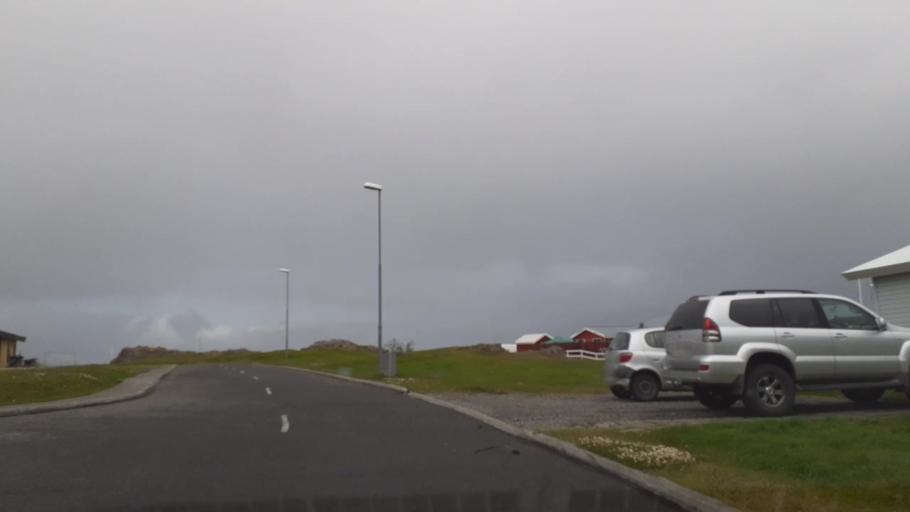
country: IS
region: East
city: Egilsstadir
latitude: 65.7539
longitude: -14.8358
